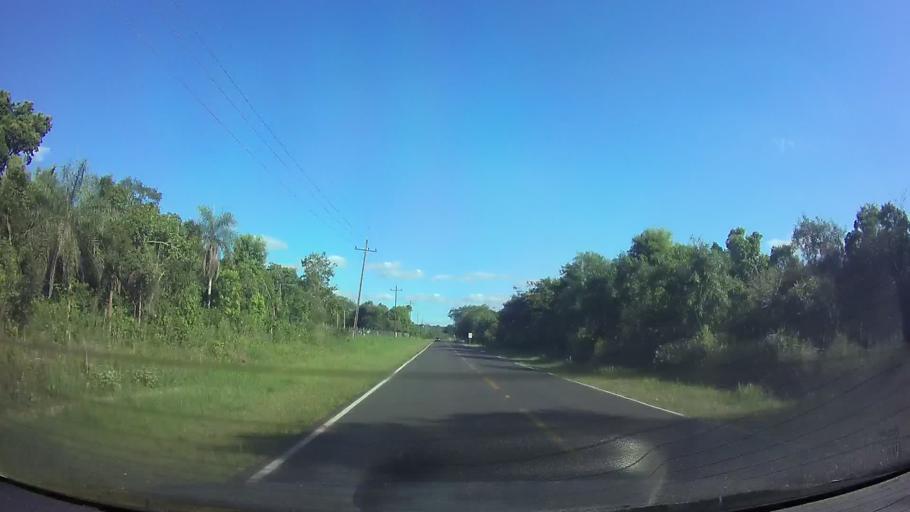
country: PY
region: Cordillera
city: Atyra
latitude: -25.2932
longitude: -57.1655
